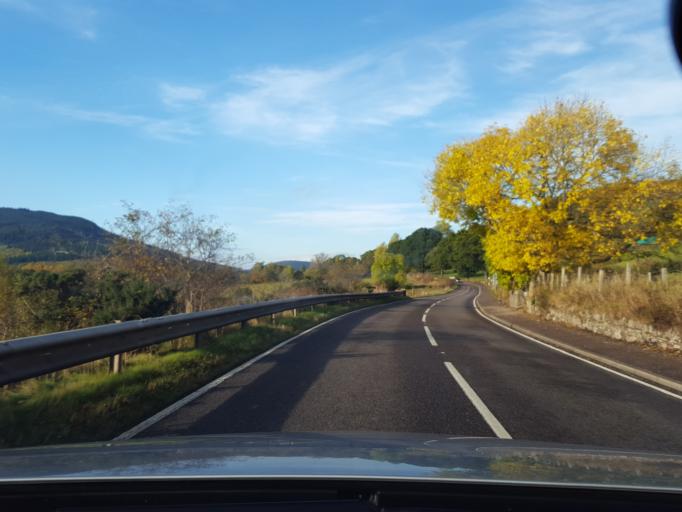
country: GB
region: Scotland
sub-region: Highland
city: Beauly
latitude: 57.3366
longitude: -4.4583
